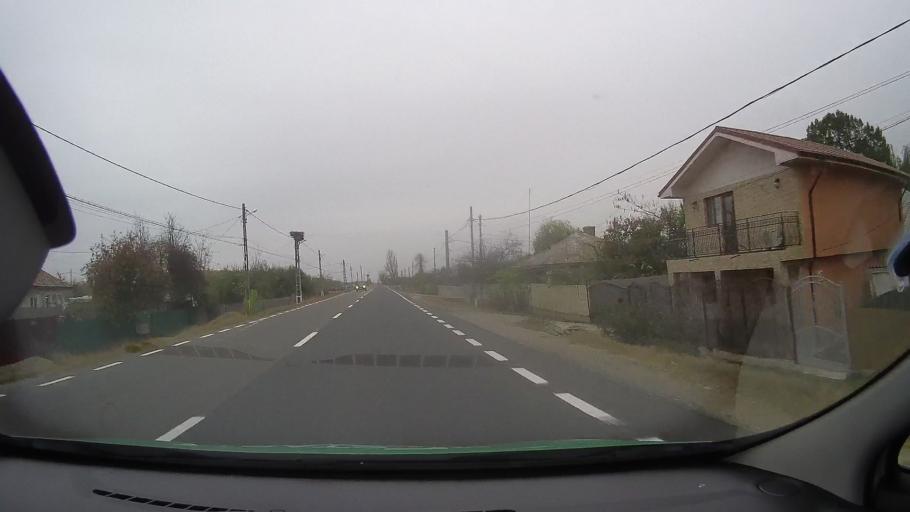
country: RO
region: Ialomita
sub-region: Comuna Giurgeni
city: Giurgeni
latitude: 44.7399
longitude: 27.8558
